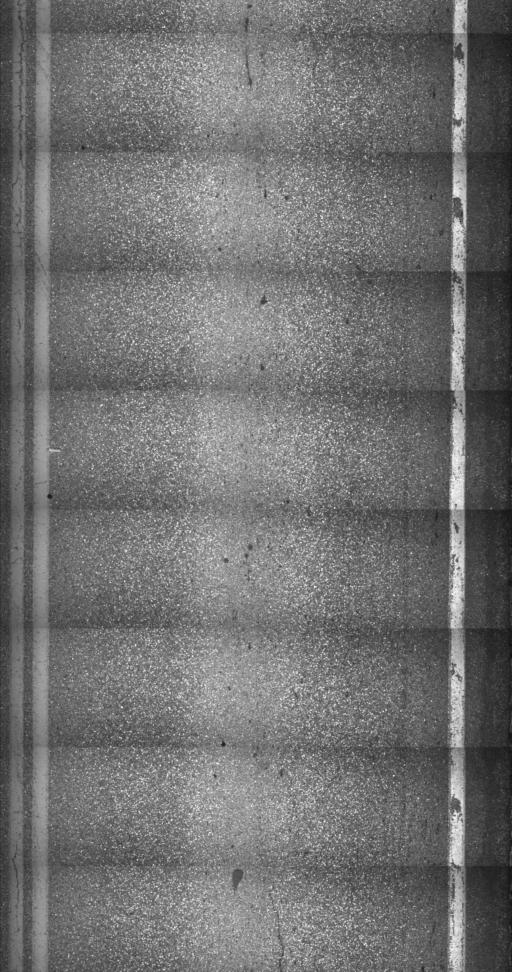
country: US
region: New York
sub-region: Essex County
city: Ticonderoga
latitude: 43.8958
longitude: -73.3089
